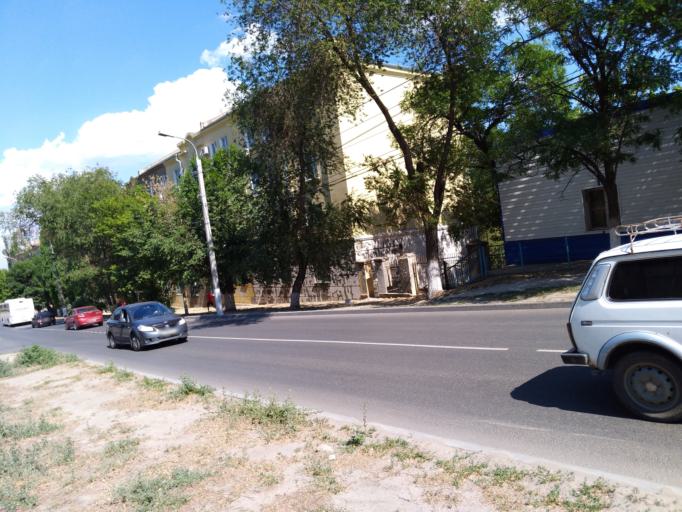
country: RU
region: Volgograd
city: Volgograd
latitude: 48.7203
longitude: 44.5236
